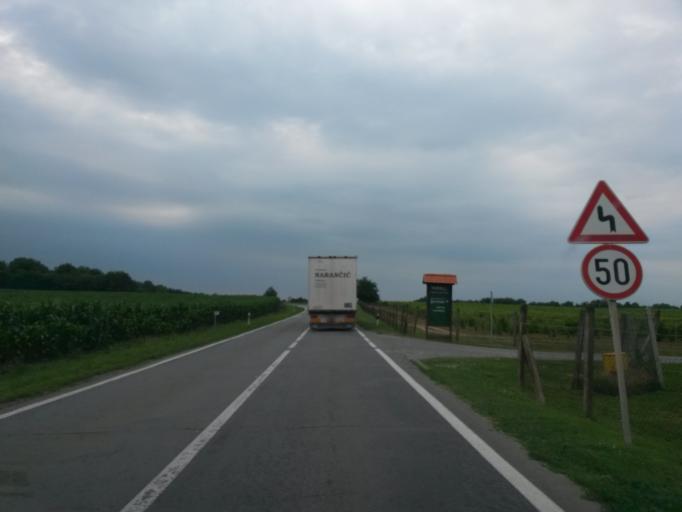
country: HR
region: Vukovarsko-Srijemska
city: Vukovar
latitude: 45.3280
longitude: 19.0521
